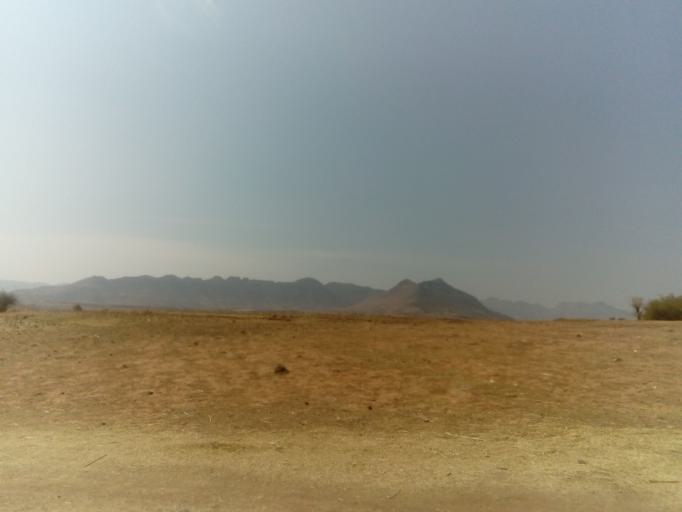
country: LS
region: Leribe
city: Leribe
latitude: -29.1329
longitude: 28.0594
